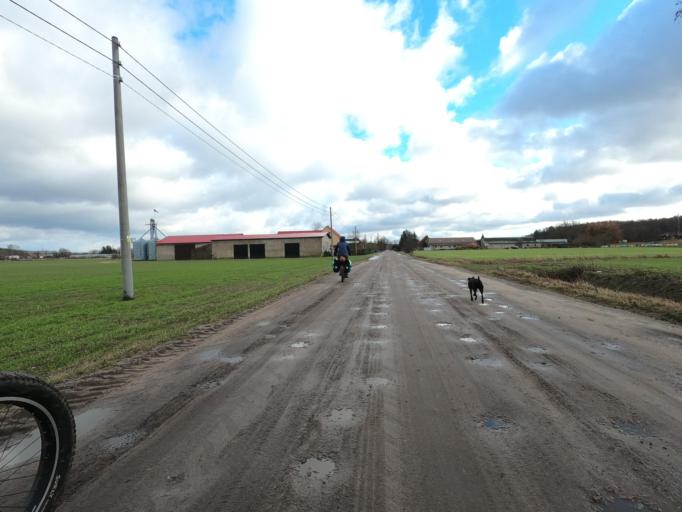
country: PL
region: Greater Poland Voivodeship
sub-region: Powiat pilski
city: Miasteczko Krajenskie
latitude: 53.1132
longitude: 16.9989
